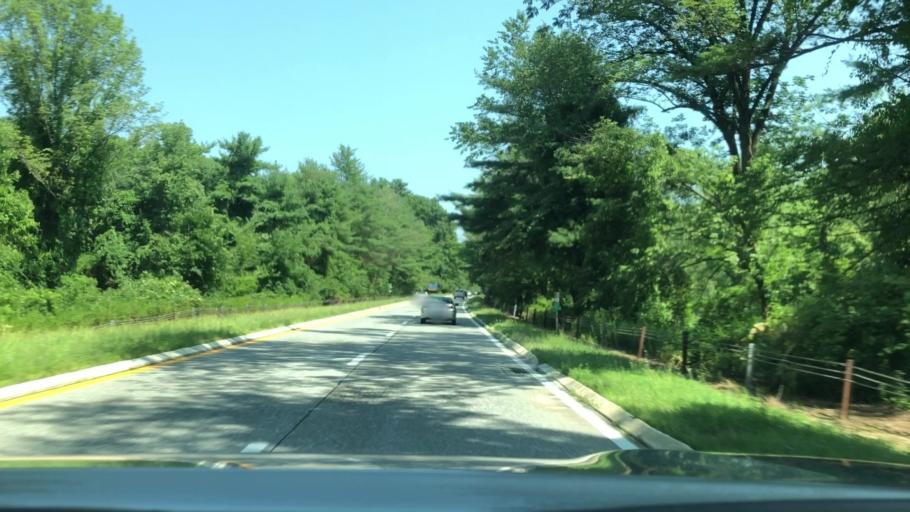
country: US
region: New York
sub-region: Rockland County
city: Stony Point
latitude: 41.2793
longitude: -74.0300
